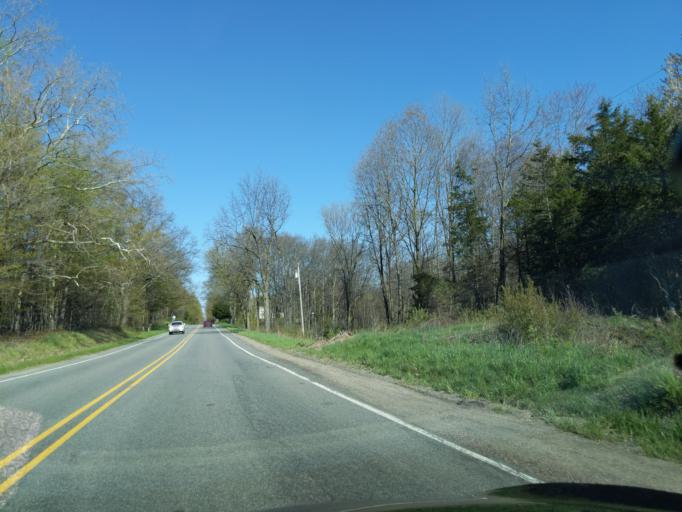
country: US
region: Michigan
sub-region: Kent County
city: Forest Hills
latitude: 42.8850
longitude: -85.4593
